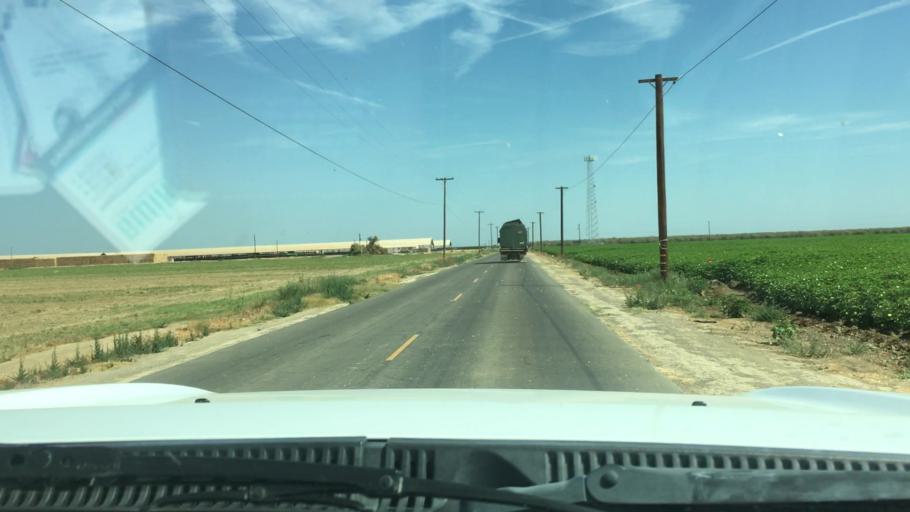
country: US
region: California
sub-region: Kern County
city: Shafter
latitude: 35.4673
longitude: -119.3681
